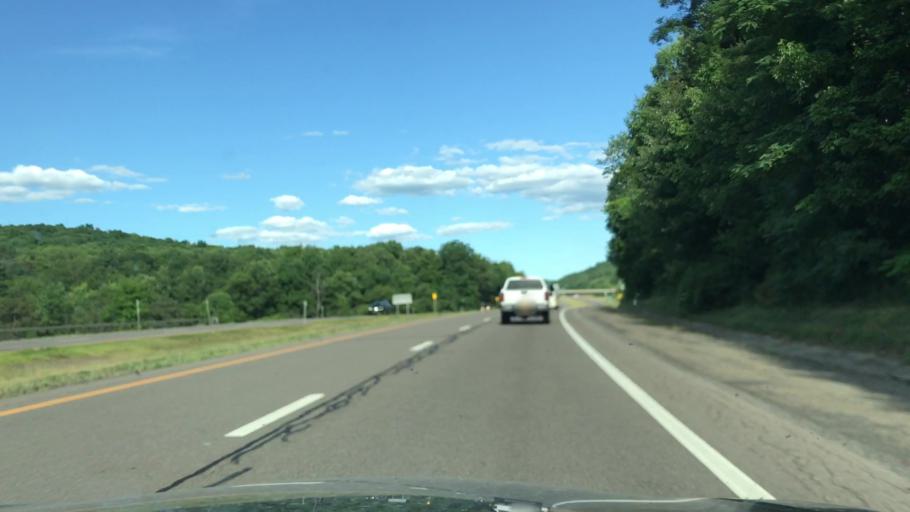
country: US
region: New York
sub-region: Broome County
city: Chenango Bridge
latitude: 42.1012
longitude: -75.8024
